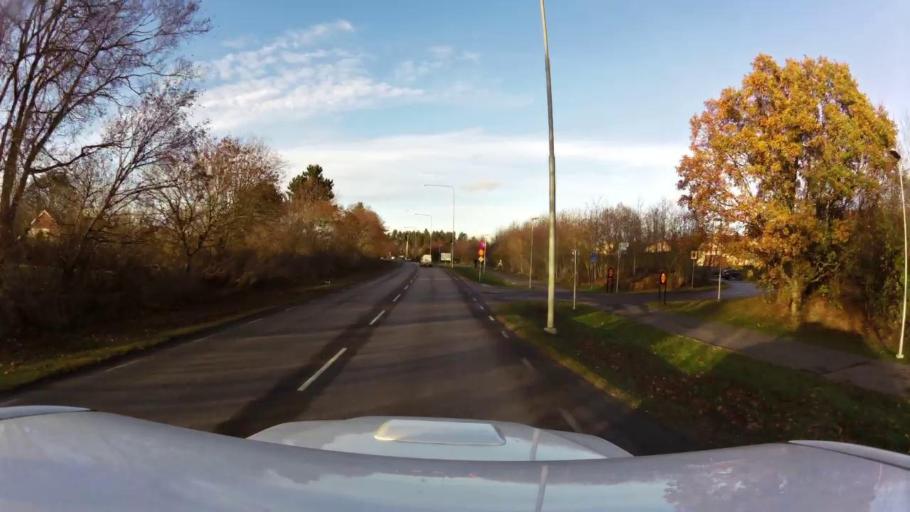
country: SE
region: OEstergoetland
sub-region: Linkopings Kommun
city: Linkoping
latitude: 58.3823
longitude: 15.6598
